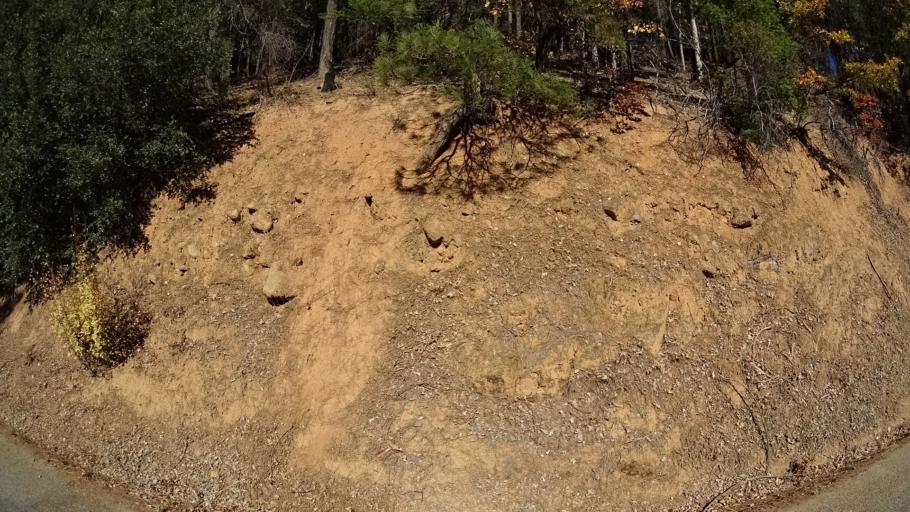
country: US
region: California
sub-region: Siskiyou County
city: Happy Camp
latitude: 41.3263
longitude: -123.0543
